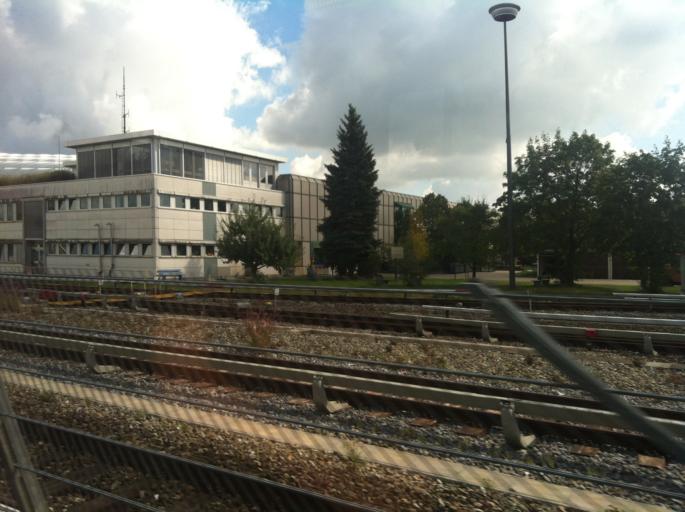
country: DE
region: Bavaria
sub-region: Upper Bavaria
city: Unterfoehring
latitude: 48.2165
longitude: 11.6195
